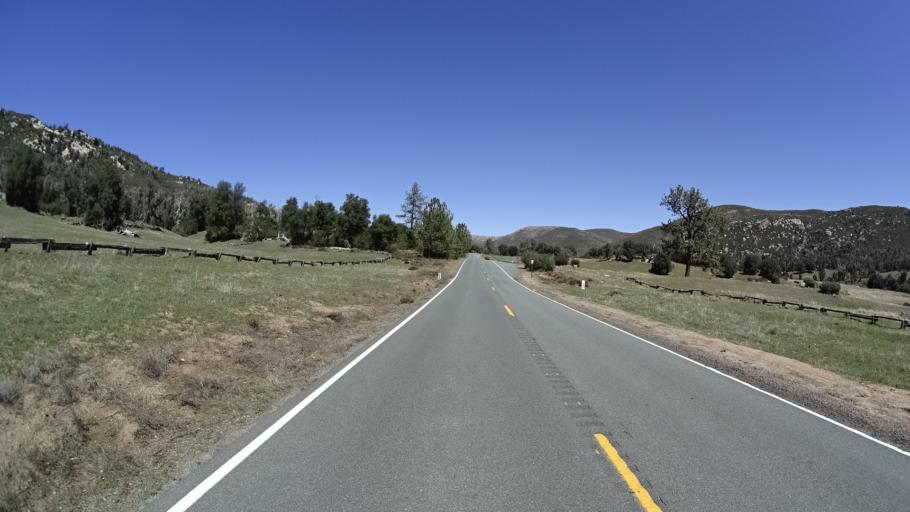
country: US
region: California
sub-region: San Diego County
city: Descanso
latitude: 32.9217
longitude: -116.5674
